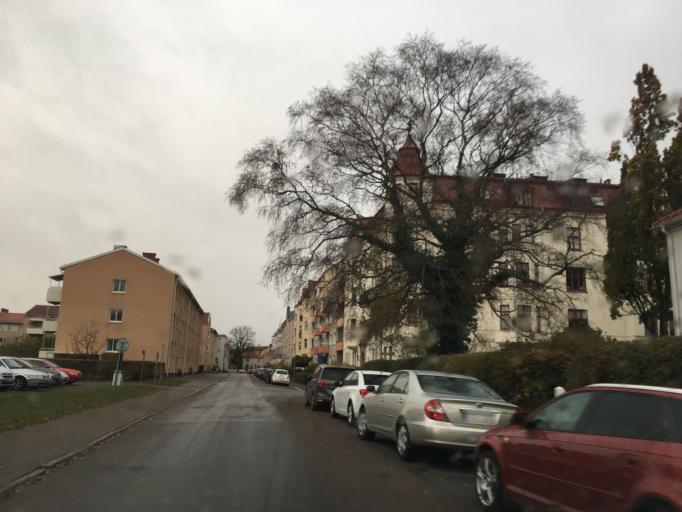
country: SE
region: Kalmar
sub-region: Kalmar Kommun
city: Kalmar
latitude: 56.6611
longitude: 16.3505
